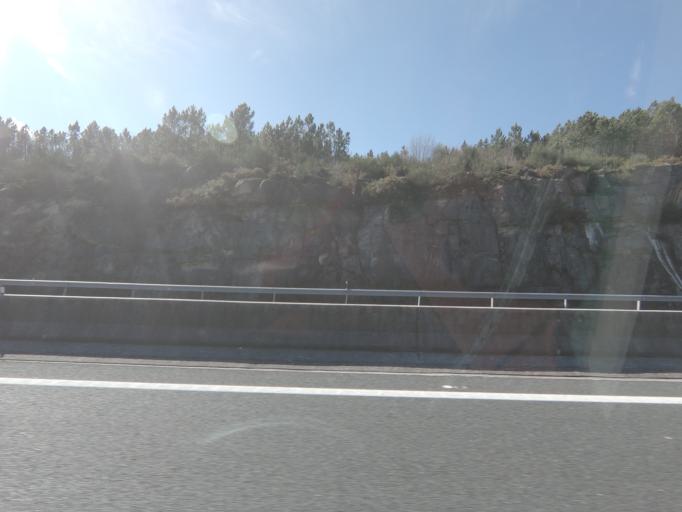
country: ES
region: Galicia
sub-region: Provincia de Ourense
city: Pinor
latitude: 42.5366
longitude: -8.0148
